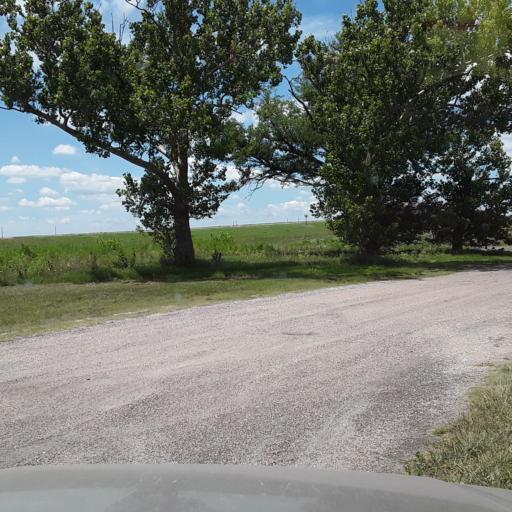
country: US
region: Nebraska
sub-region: Merrick County
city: Central City
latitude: 41.1918
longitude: -97.8723
